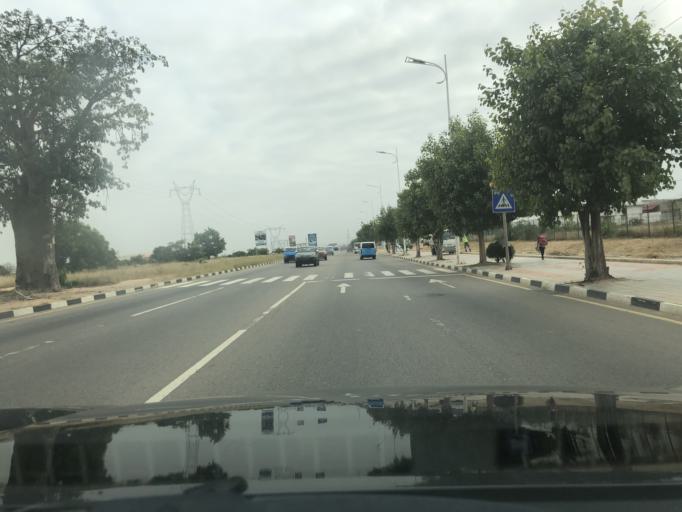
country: AO
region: Luanda
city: Luanda
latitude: -8.9842
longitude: 13.2902
